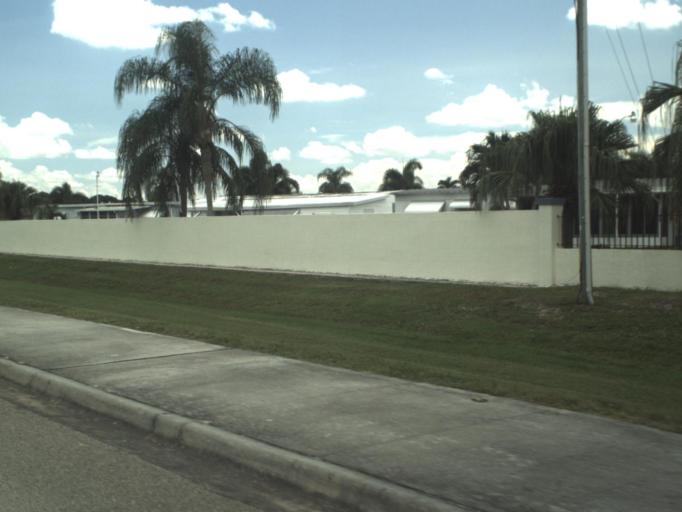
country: US
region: Florida
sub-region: Martin County
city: Palm City
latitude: 27.1639
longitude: -80.2493
